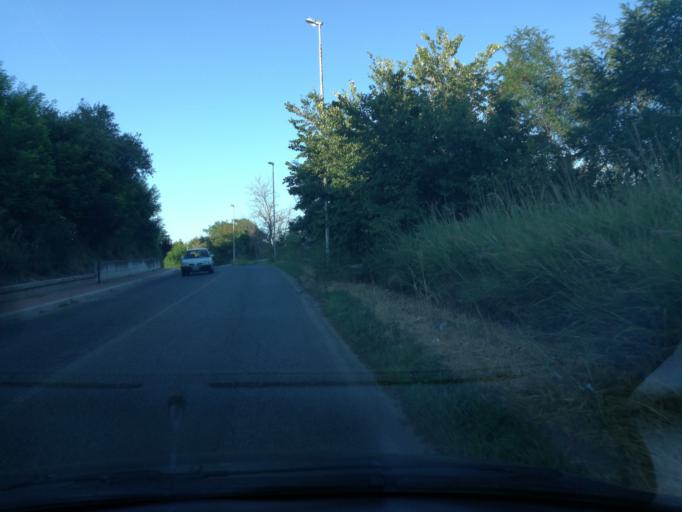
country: IT
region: Molise
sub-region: Provincia di Campobasso
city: Guglionesi
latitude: 41.9191
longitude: 14.9153
